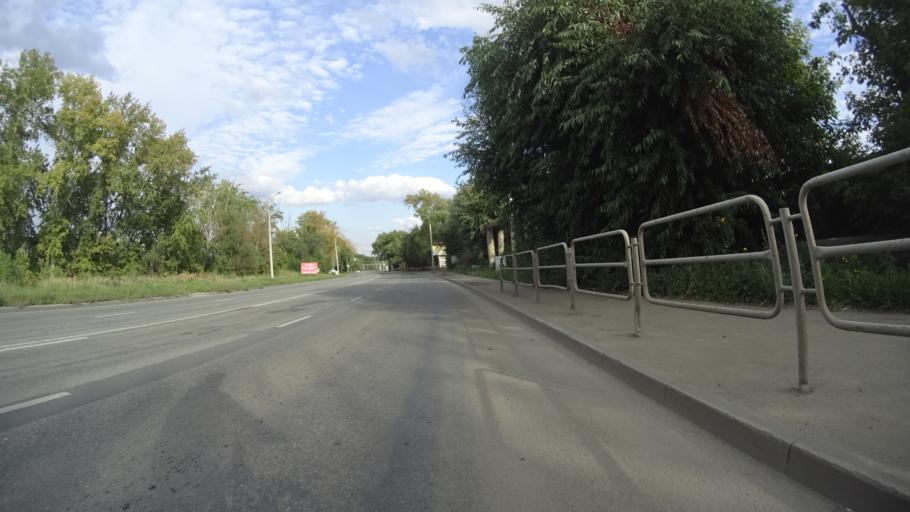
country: RU
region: Chelyabinsk
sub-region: Gorod Chelyabinsk
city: Chelyabinsk
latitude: 55.1961
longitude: 61.3761
